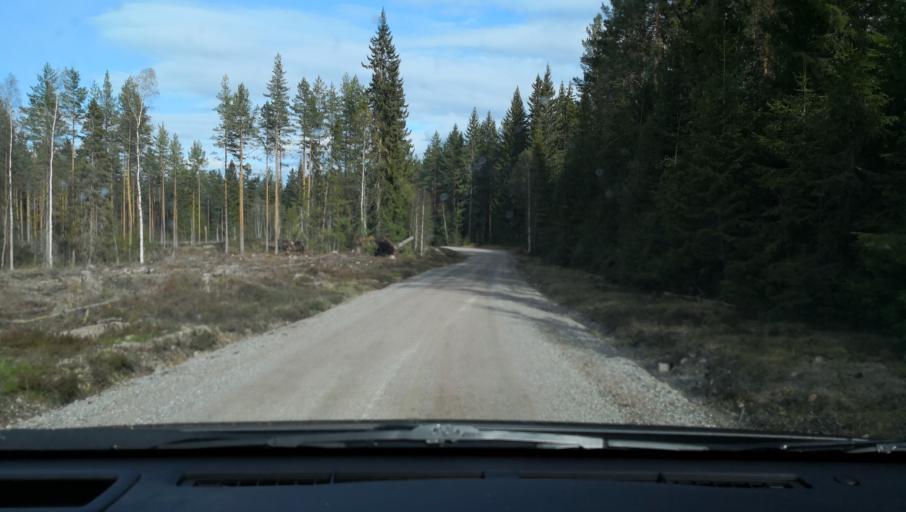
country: SE
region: Dalarna
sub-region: Saters Kommun
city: Saeter
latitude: 60.1710
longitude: 15.7219
